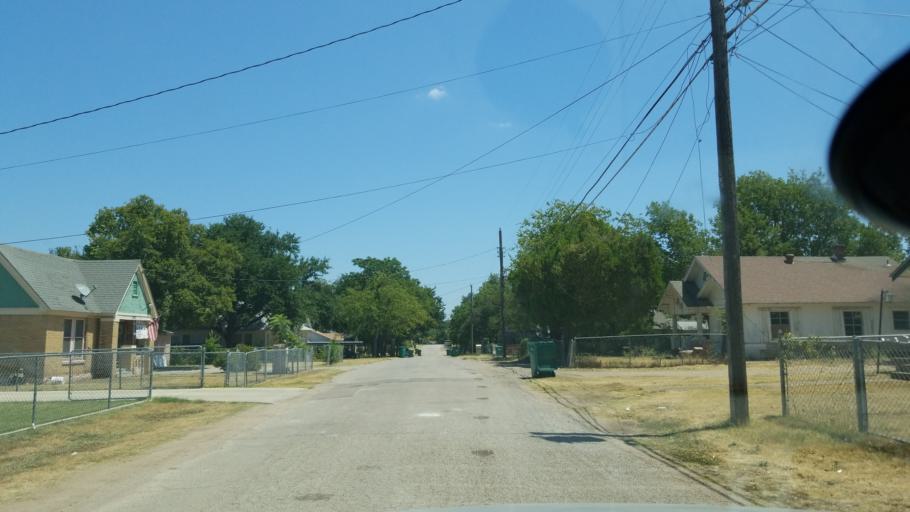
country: US
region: Texas
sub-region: Dallas County
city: Cockrell Hill
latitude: 32.7375
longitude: -96.8839
